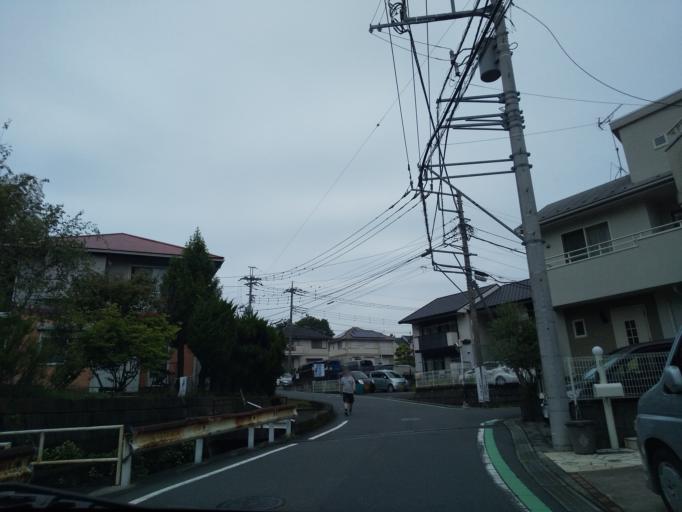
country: JP
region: Tokyo
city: Hino
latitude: 35.6493
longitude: 139.4266
